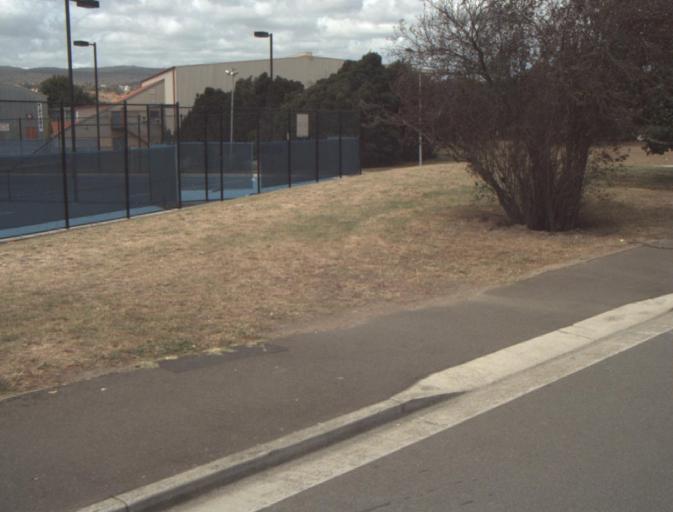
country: AU
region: Tasmania
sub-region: Launceston
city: East Launceston
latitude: -41.4317
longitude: 147.1507
